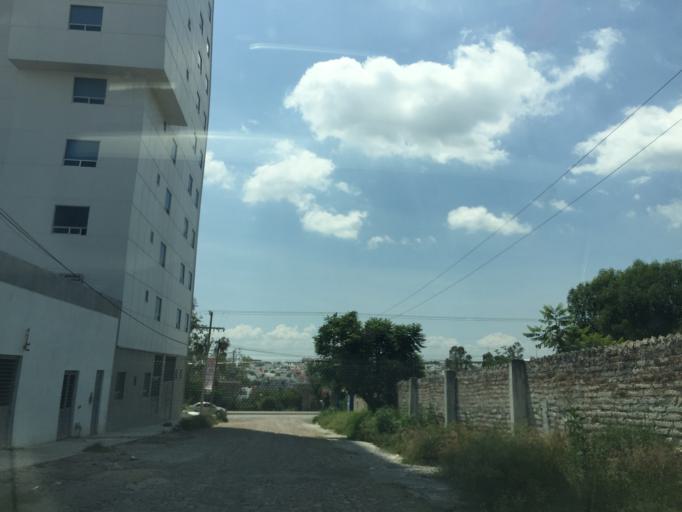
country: MX
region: Guanajuato
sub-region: Leon
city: La Ermita
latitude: 21.1594
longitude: -101.7224
